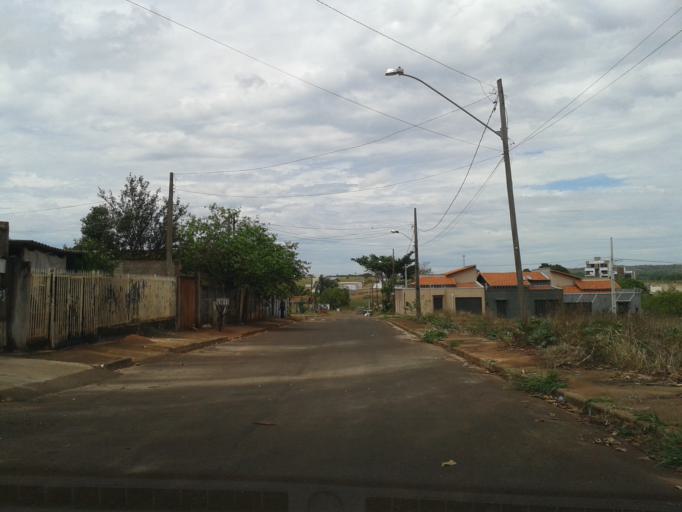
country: BR
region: Minas Gerais
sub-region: Ituiutaba
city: Ituiutaba
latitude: -18.9956
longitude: -49.4623
